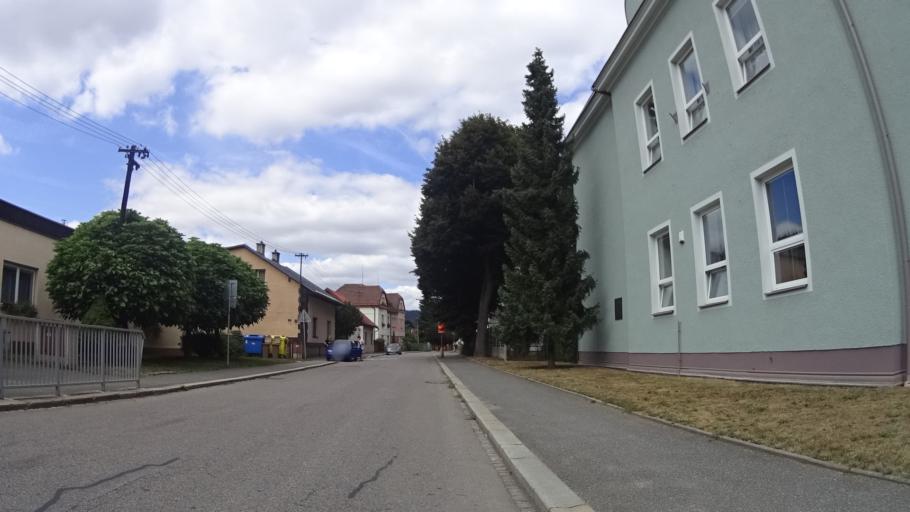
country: CZ
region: Pardubicky
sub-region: Okres Usti nad Orlici
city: Usti nad Orlici
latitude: 49.9702
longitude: 16.3688
